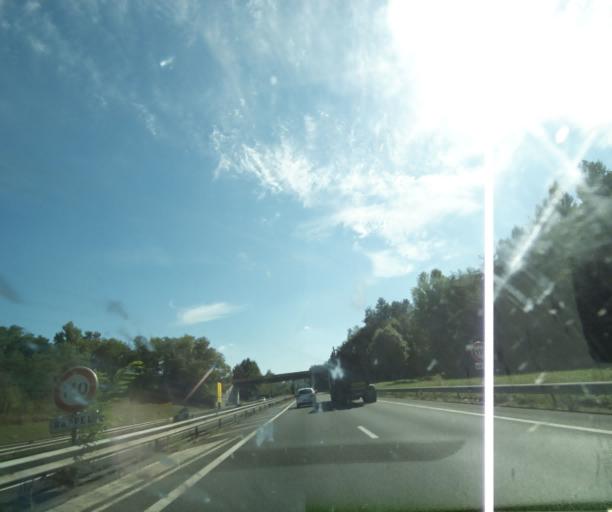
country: FR
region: Limousin
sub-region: Departement de la Correze
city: Saint-Pantaleon-de-Larche
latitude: 45.1458
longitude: 1.4856
